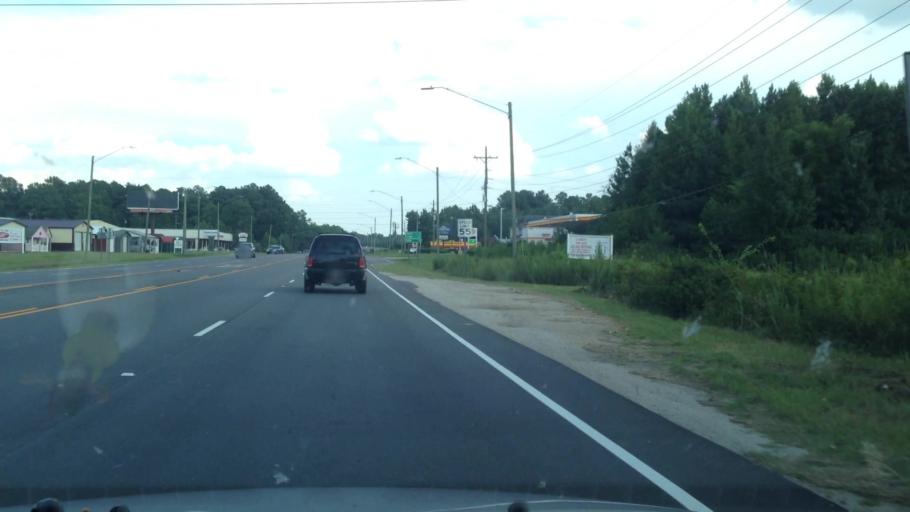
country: US
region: North Carolina
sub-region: Harnett County
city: Lillington
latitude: 35.4168
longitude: -78.8013
